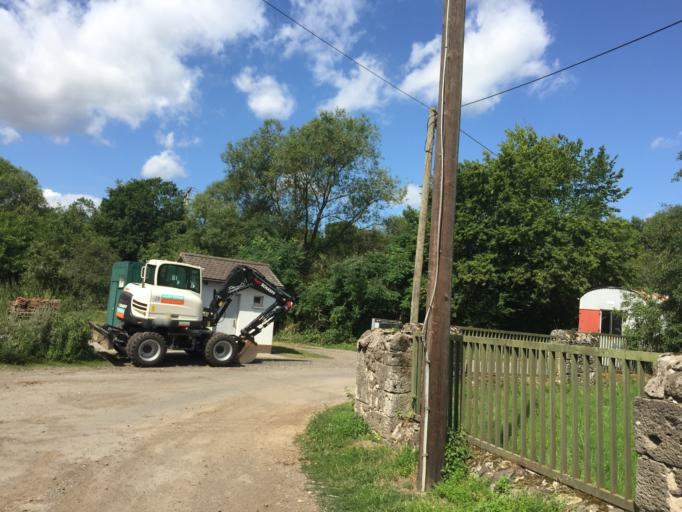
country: DE
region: Hesse
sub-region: Regierungsbezirk Giessen
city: Grunberg
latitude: 50.5706
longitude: 8.9767
